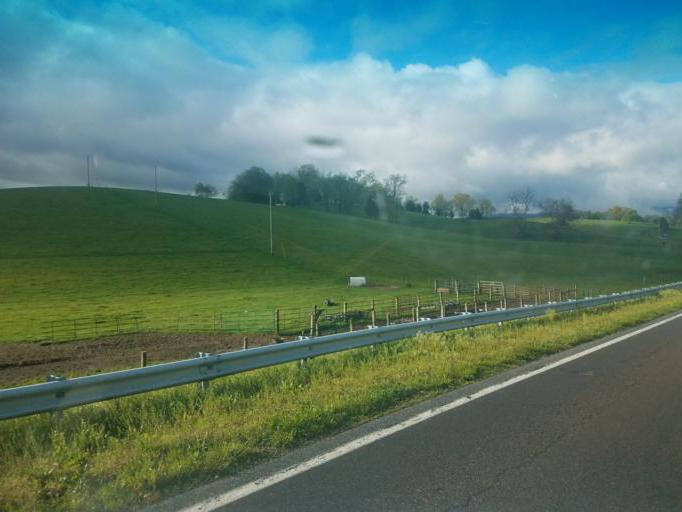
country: US
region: Virginia
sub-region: Washington County
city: Emory
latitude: 36.6921
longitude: -81.8048
